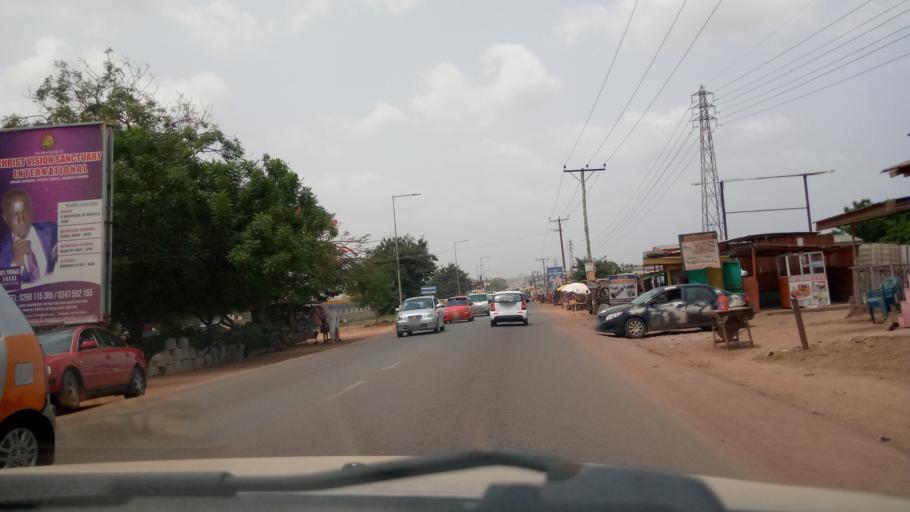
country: GH
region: Greater Accra
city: Dome
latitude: 5.6677
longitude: -0.2359
